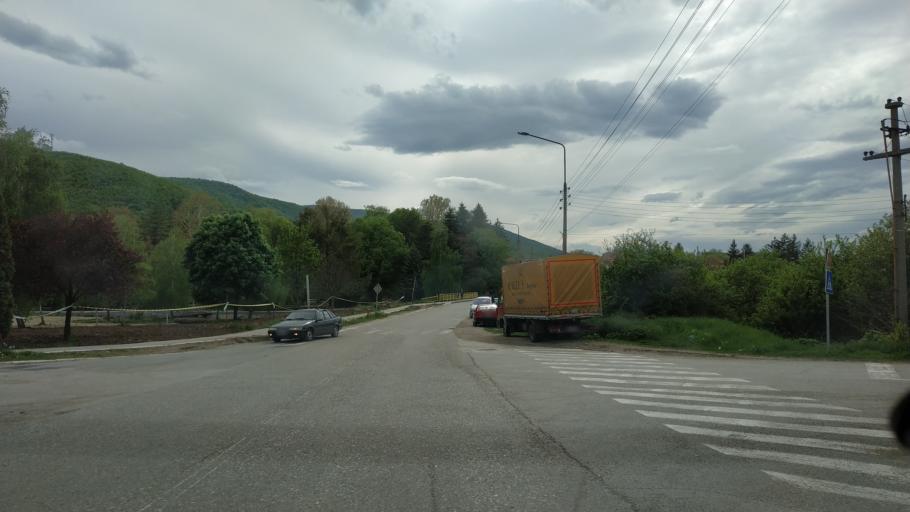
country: RS
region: Central Serbia
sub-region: Zajecarski Okrug
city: Soko Banja
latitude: 43.6457
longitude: 21.8822
